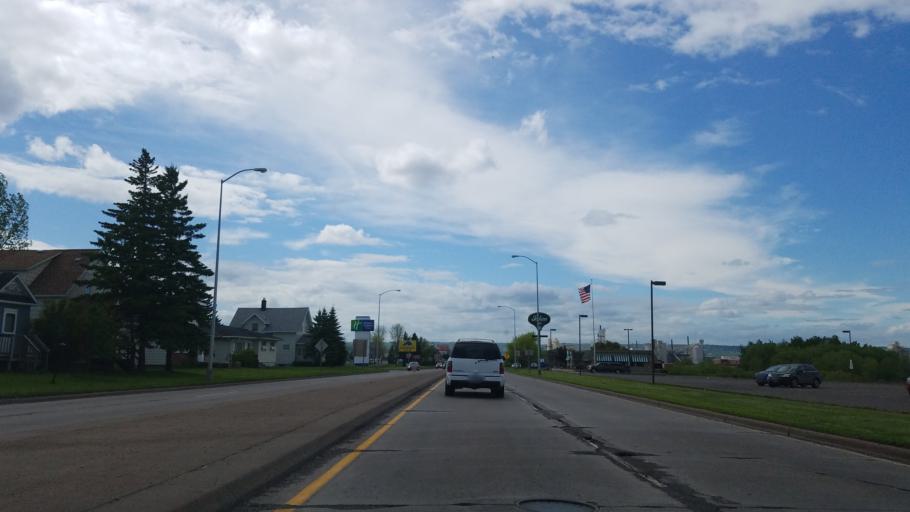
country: US
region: Wisconsin
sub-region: Douglas County
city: Superior
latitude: 46.7227
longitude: -92.0691
